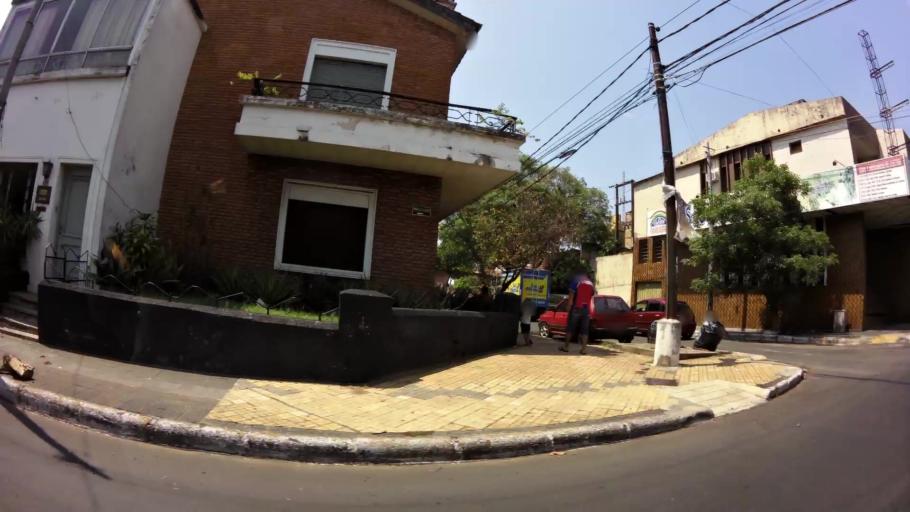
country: PY
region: Asuncion
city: Asuncion
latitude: -25.2840
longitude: -57.6433
